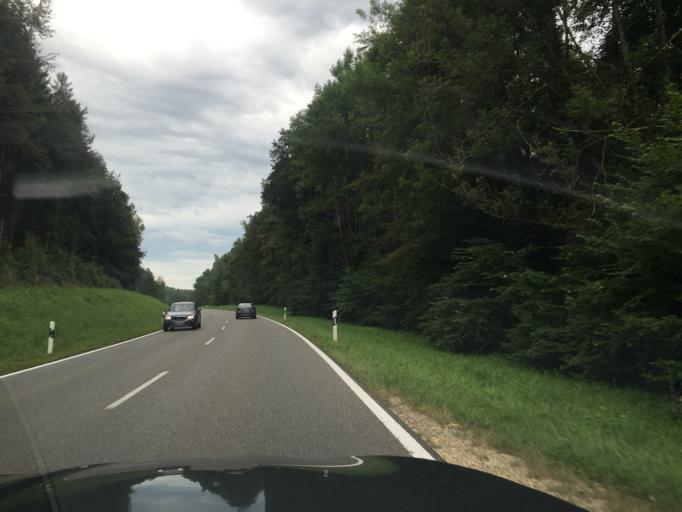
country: DE
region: Baden-Wuerttemberg
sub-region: Freiburg Region
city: Stockach
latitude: 47.8346
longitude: 8.9903
